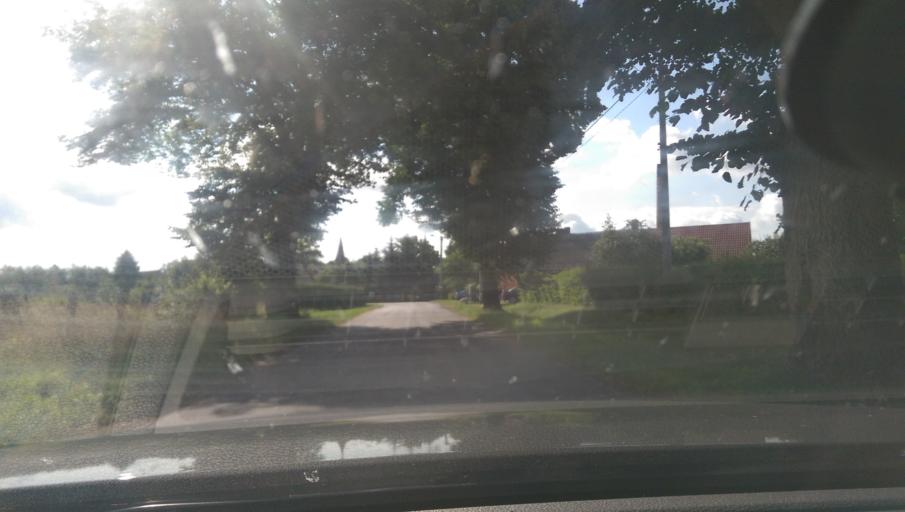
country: PL
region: West Pomeranian Voivodeship
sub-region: Powiat walecki
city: Walcz
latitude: 53.3503
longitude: 16.5679
